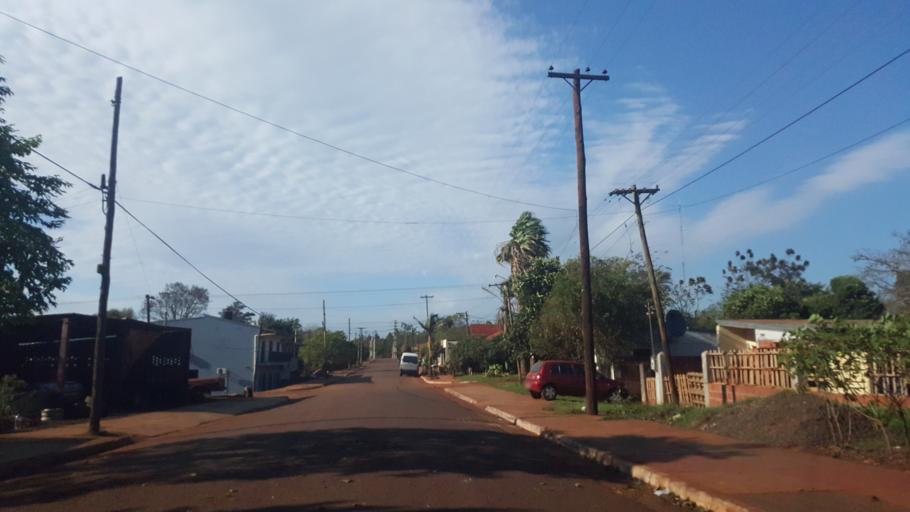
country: AR
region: Misiones
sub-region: Departamento de San Ignacio
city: San Ignacio
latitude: -27.2540
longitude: -55.5284
